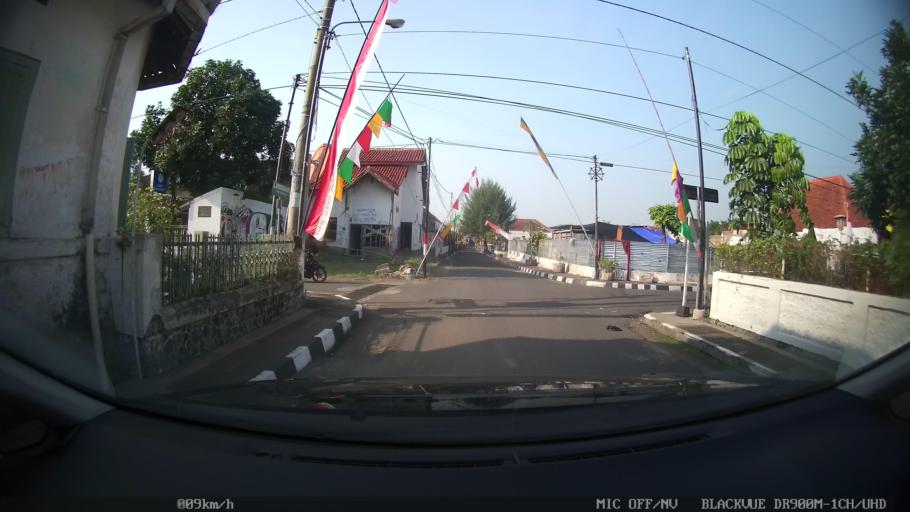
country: ID
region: Daerah Istimewa Yogyakarta
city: Yogyakarta
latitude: -7.8060
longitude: 110.3678
